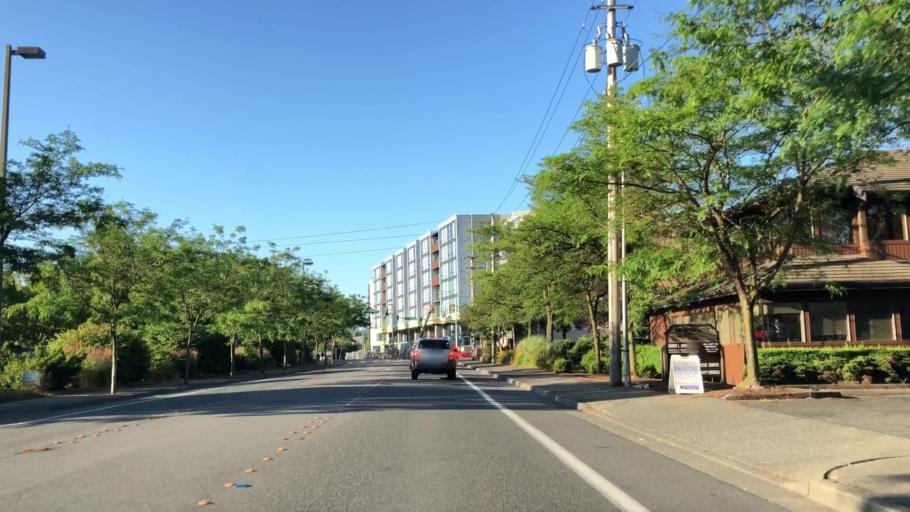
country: US
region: Washington
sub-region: King County
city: Redmond
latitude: 47.6759
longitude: -122.1192
